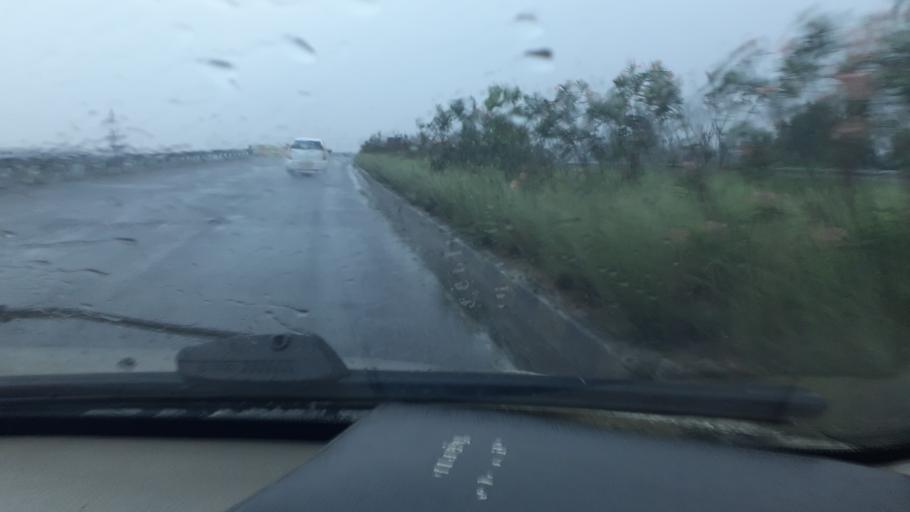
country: IN
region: Tamil Nadu
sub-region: Virudhunagar
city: Sattur
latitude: 9.3809
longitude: 77.9137
